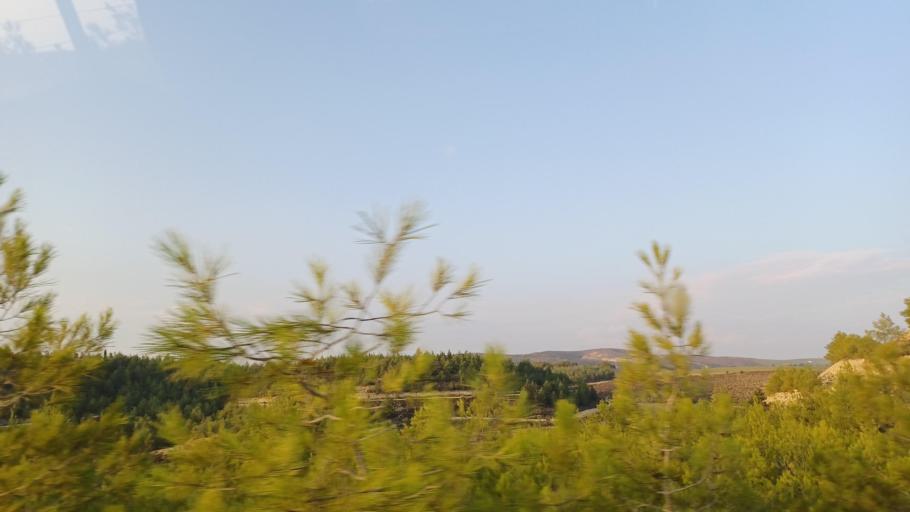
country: CY
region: Lefkosia
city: Lympia
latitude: 34.9961
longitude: 33.5247
